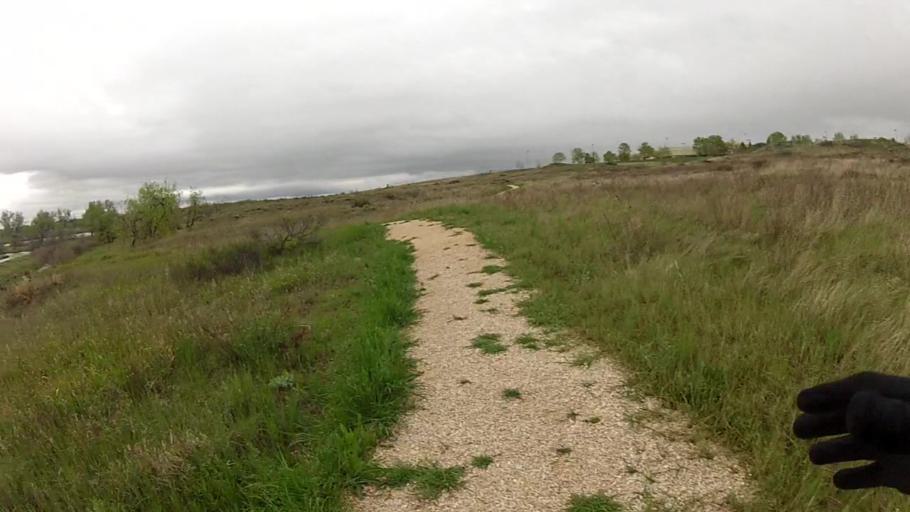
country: US
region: Colorado
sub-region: Larimer County
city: Loveland
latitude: 40.3838
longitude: -105.0942
